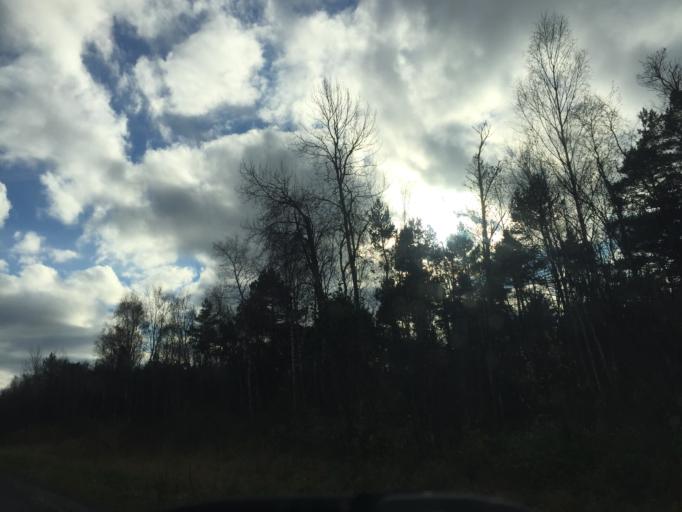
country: LV
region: Liepaja
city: Vec-Liepaja
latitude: 56.5670
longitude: 21.0539
